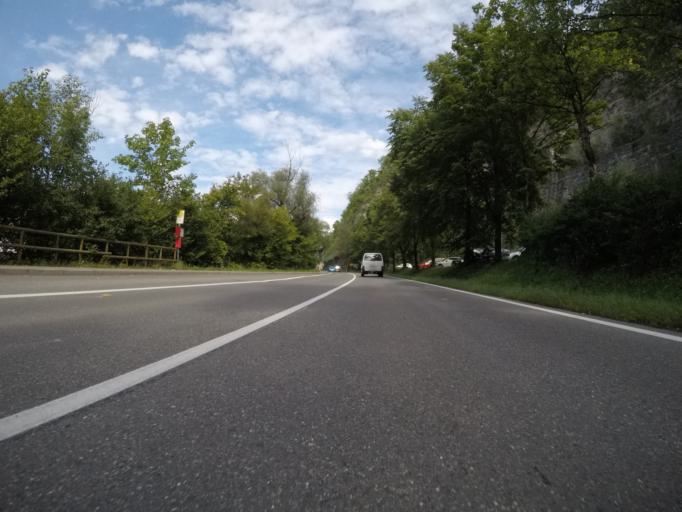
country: DE
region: Baden-Wuerttemberg
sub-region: Tuebingen Region
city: Rottenburg
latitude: 48.4659
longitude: 8.9202
